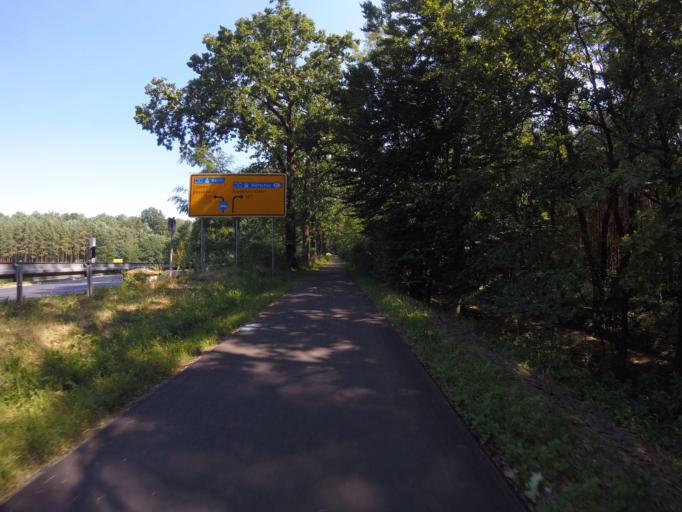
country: DE
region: Brandenburg
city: Mullrose
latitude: 52.2699
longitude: 14.4385
